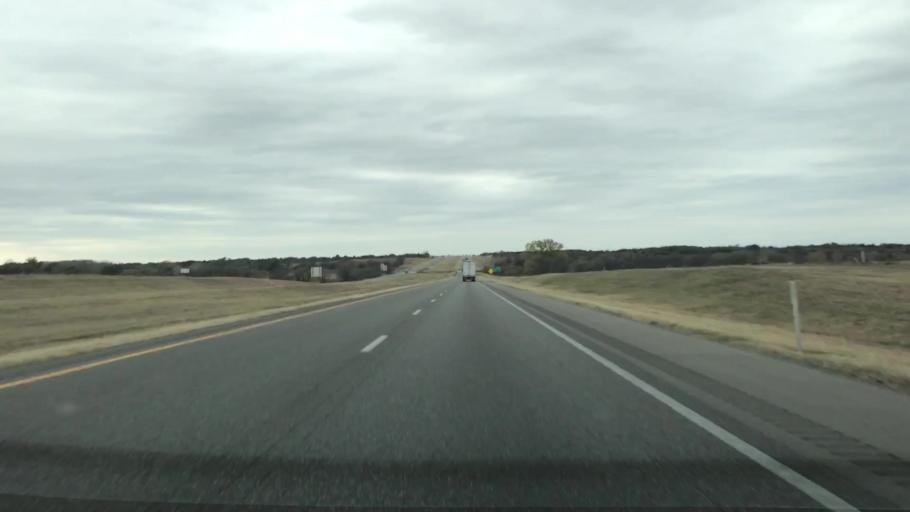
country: US
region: Oklahoma
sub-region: Beckham County
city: Erick
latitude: 35.2266
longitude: -99.8874
